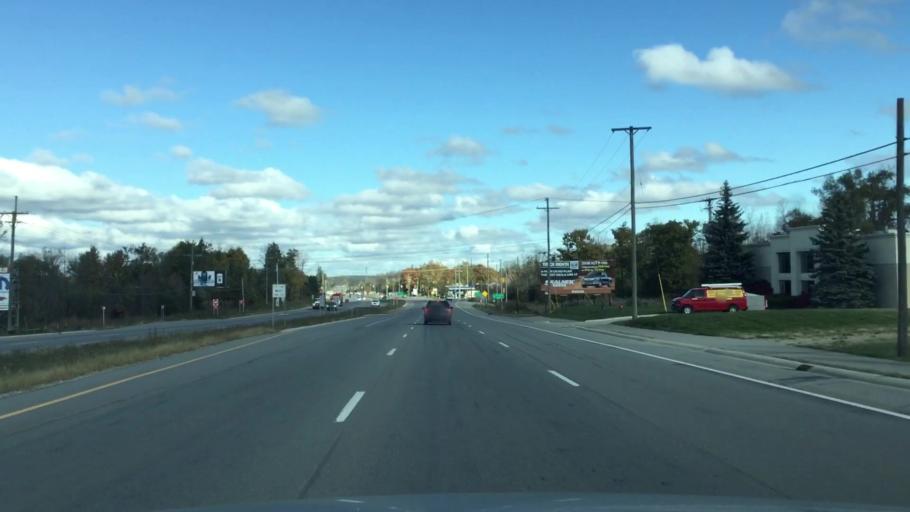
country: US
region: Michigan
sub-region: Oakland County
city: Auburn Hills
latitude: 42.7194
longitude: -83.2425
